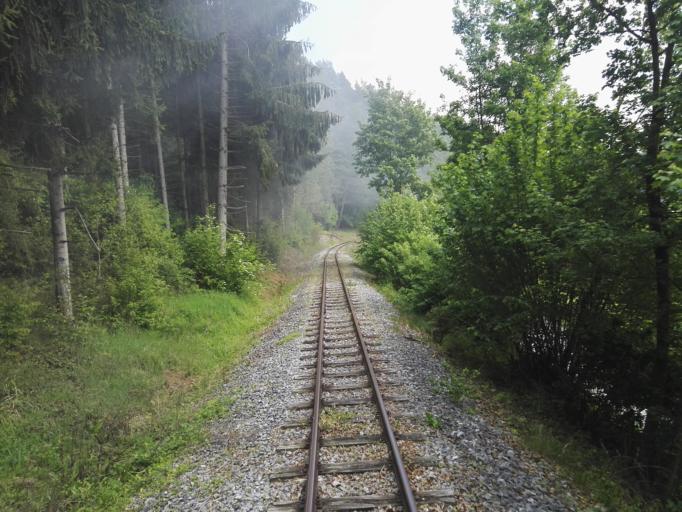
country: AT
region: Styria
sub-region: Politischer Bezirk Weiz
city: Anger
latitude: 47.2663
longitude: 15.7069
